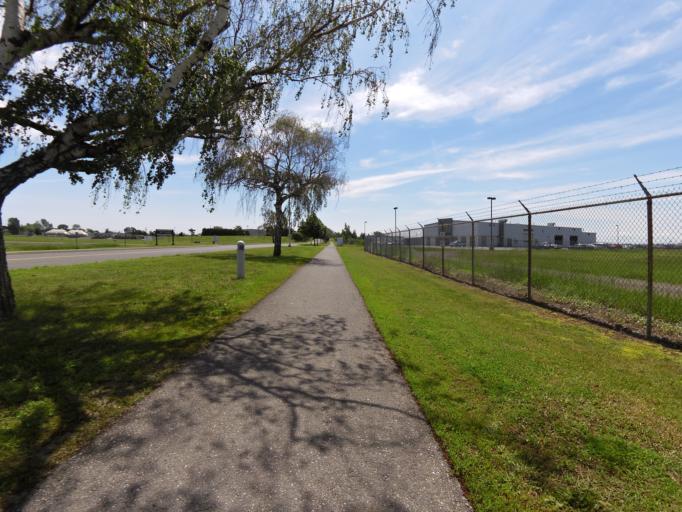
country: CA
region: Ontario
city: Ottawa
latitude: 45.3354
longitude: -75.6820
